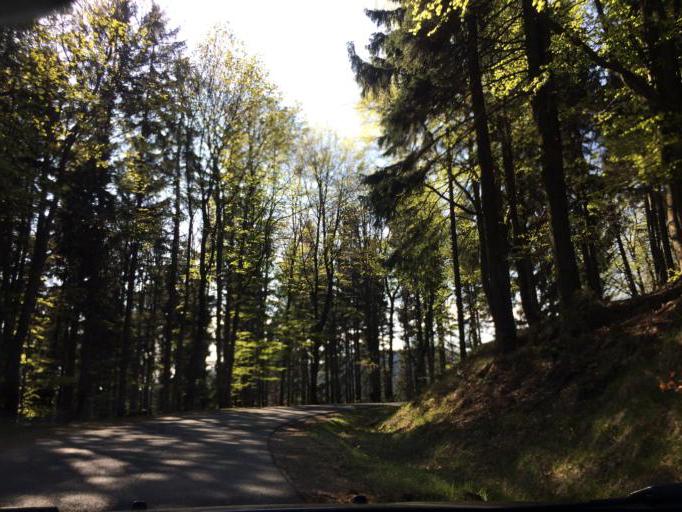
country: PL
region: Lower Silesian Voivodeship
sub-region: Powiat klodzki
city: Jugow
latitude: 50.6627
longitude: 16.5232
